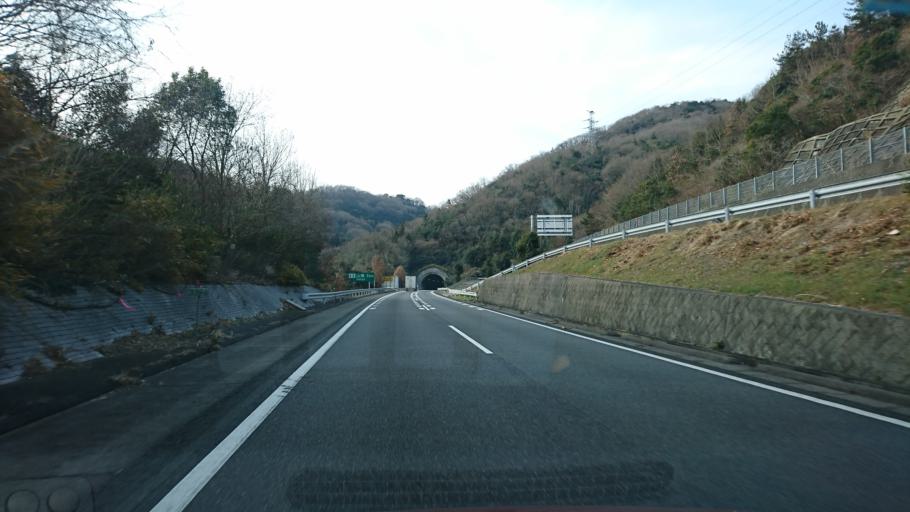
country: JP
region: Okayama
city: Okayama-shi
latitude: 34.7593
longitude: 134.0554
